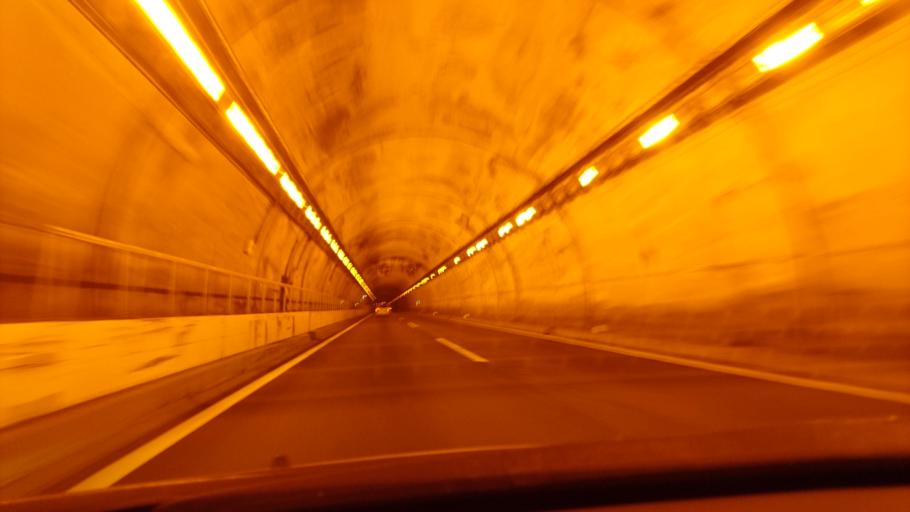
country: JP
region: Akita
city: Hanawa
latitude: 40.0186
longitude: 140.9856
